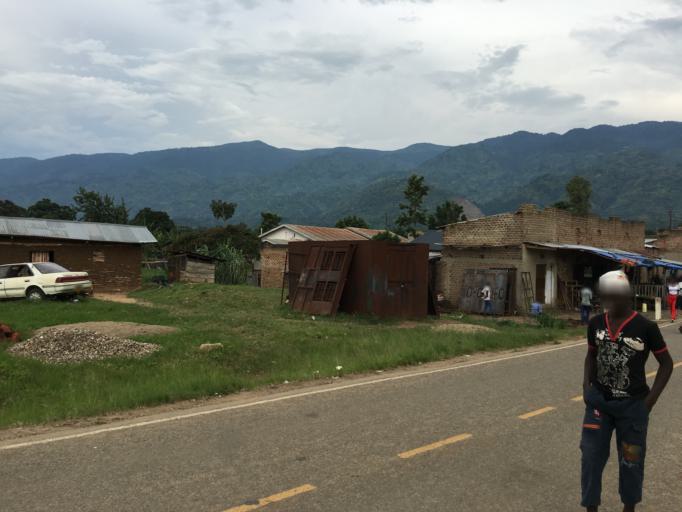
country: UG
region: Western Region
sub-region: Bundibugyo District
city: Bundibugyo
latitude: 0.7080
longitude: 30.0643
